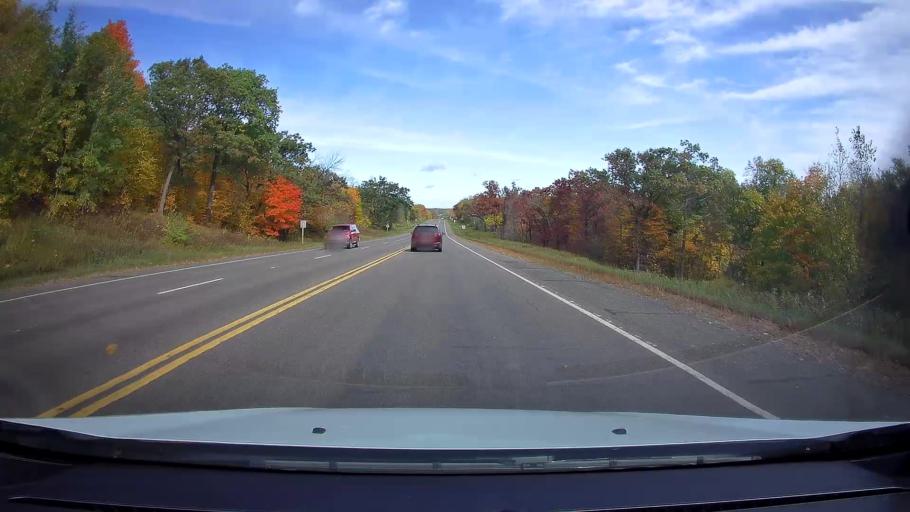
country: US
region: Wisconsin
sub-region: Polk County
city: Saint Croix Falls
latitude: 45.3813
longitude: -92.6366
